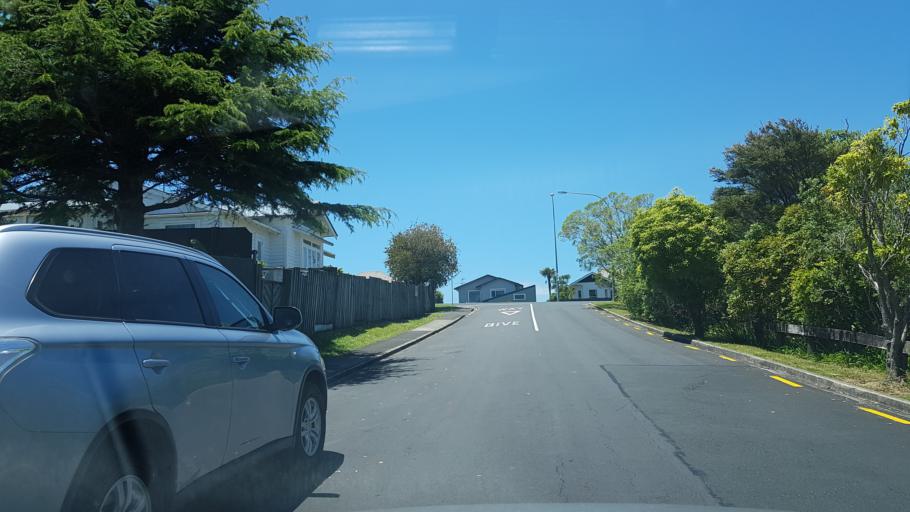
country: NZ
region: Auckland
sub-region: Auckland
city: North Shore
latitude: -36.8055
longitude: 174.7246
